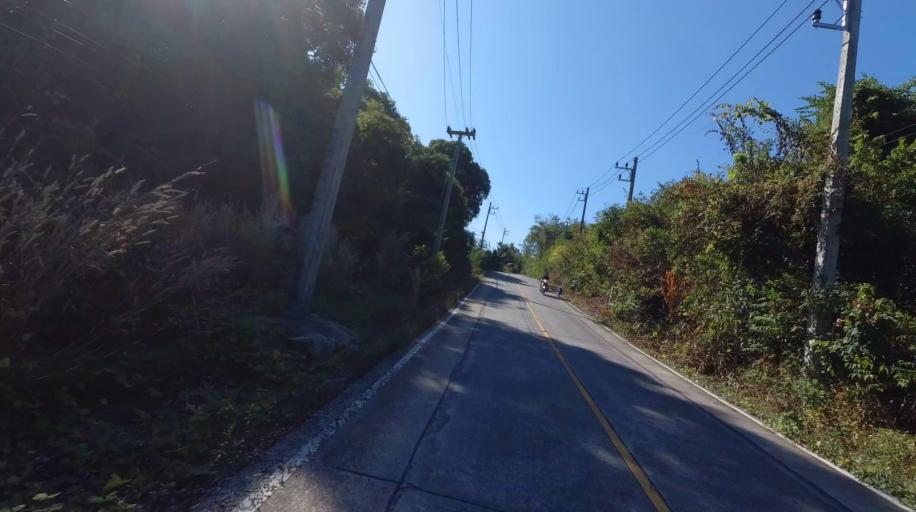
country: TH
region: Trat
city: Ko Kut
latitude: 11.6160
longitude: 102.5435
